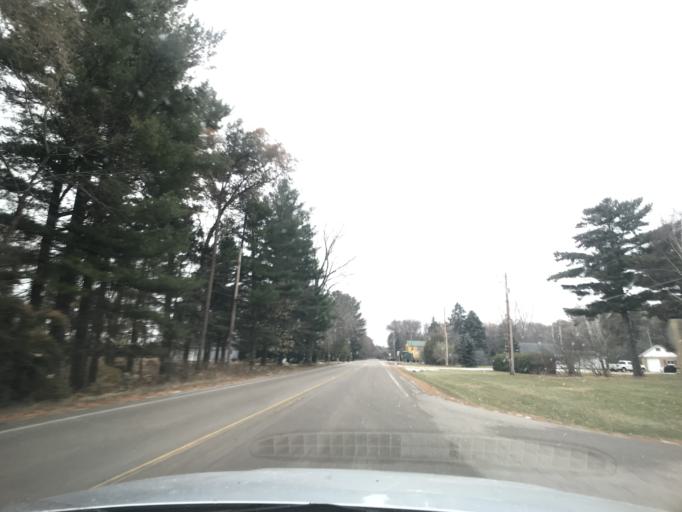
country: US
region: Wisconsin
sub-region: Marinette County
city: Marinette
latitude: 45.0616
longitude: -87.6197
